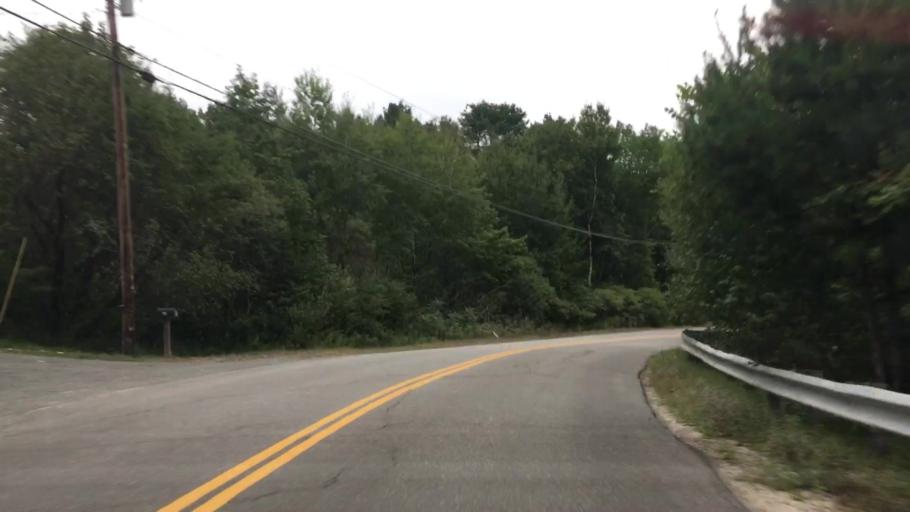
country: US
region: Maine
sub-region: Cumberland County
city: New Gloucester
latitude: 43.9015
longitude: -70.2042
